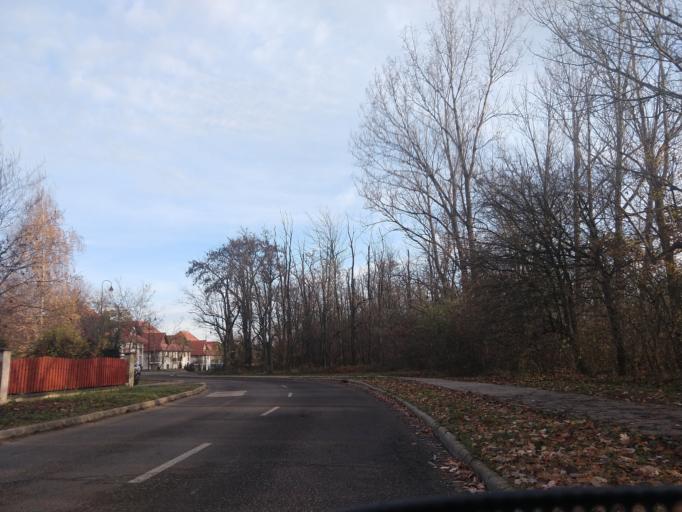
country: HU
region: Pest
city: Orbottyan
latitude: 47.6606
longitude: 19.2701
